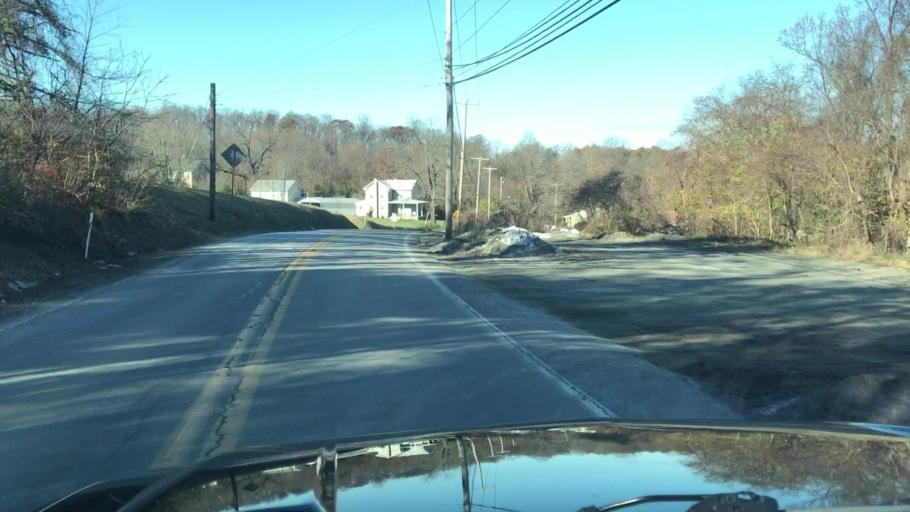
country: US
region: Pennsylvania
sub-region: Cumberland County
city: Lower Allen
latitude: 40.1820
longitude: -76.8806
